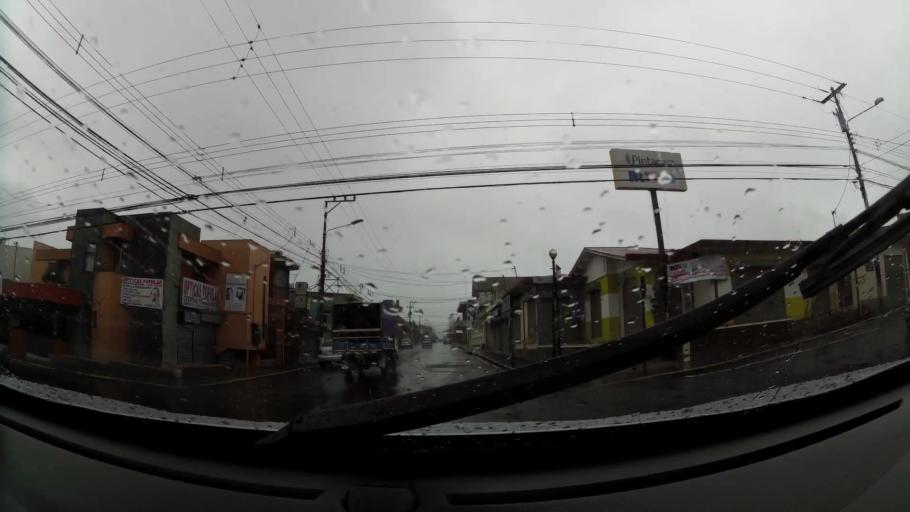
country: CR
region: Cartago
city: Cartago
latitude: 9.8650
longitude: -83.9165
